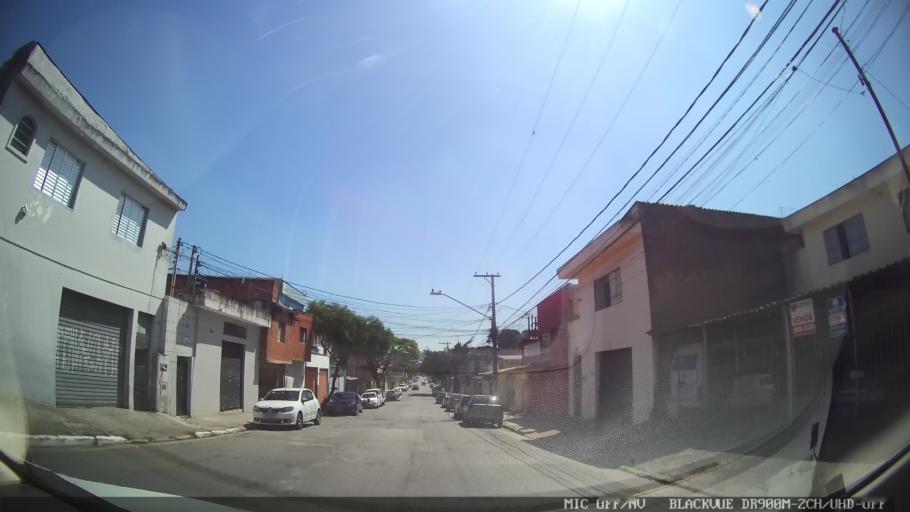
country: BR
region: Sao Paulo
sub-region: Sao Paulo
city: Sao Paulo
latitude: -23.4998
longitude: -46.6575
